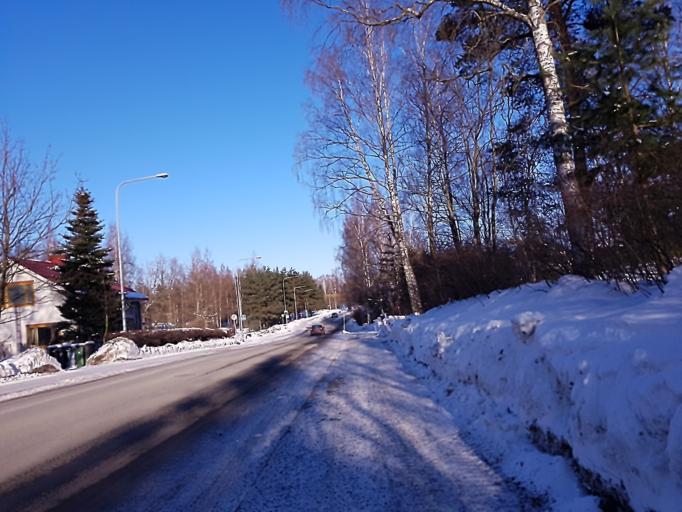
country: FI
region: Uusimaa
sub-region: Helsinki
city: Teekkarikylae
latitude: 60.2460
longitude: 24.8820
